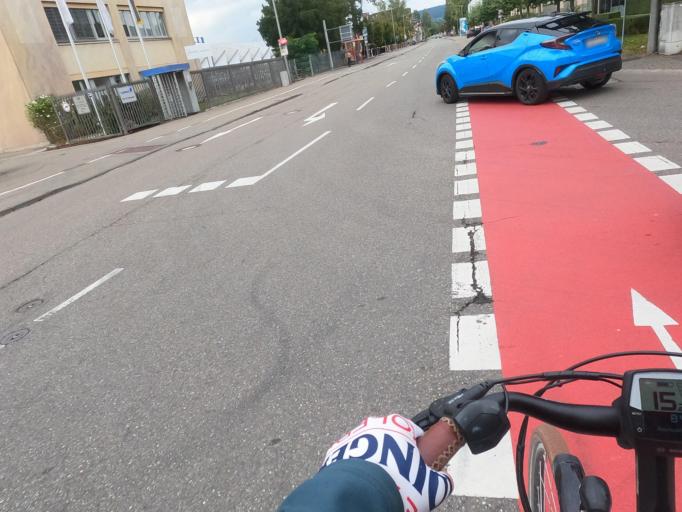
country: DE
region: Baden-Wuerttemberg
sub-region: Freiburg Region
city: Radolfzell am Bodensee
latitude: 47.7399
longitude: 8.9695
